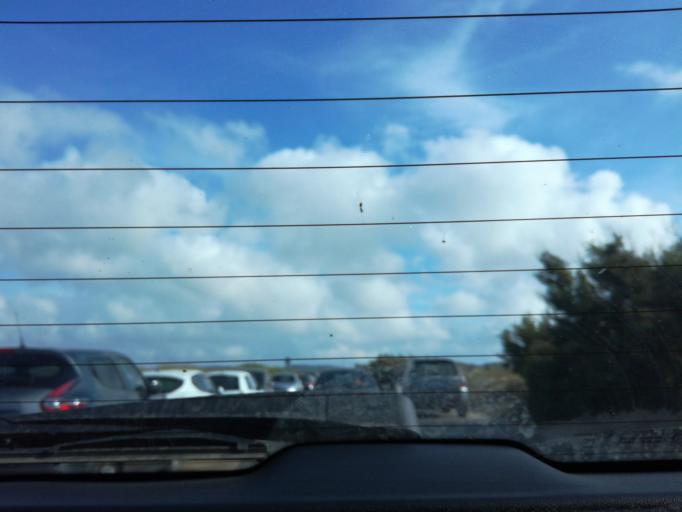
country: FR
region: Provence-Alpes-Cote d'Azur
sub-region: Departement du Var
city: Hyeres
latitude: 43.0640
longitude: 6.1314
